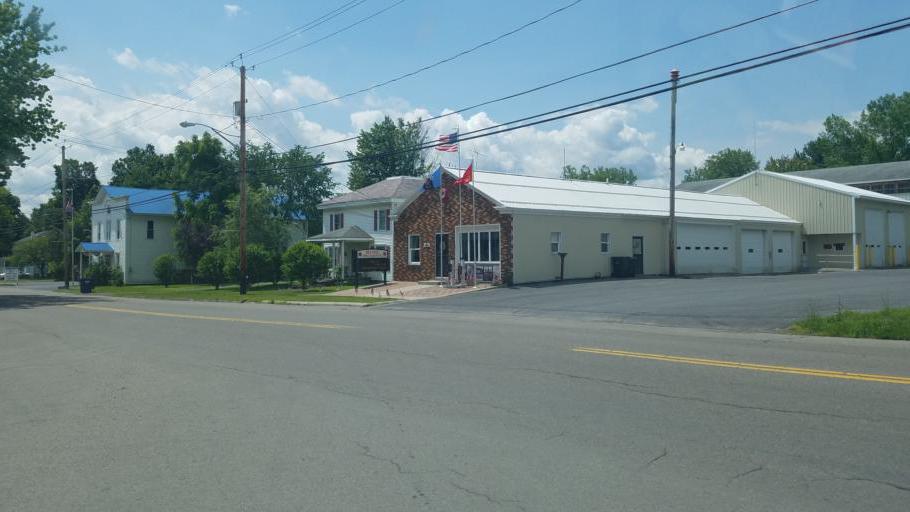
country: US
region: New York
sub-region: Wayne County
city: Clyde
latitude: 43.1537
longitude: -76.8783
